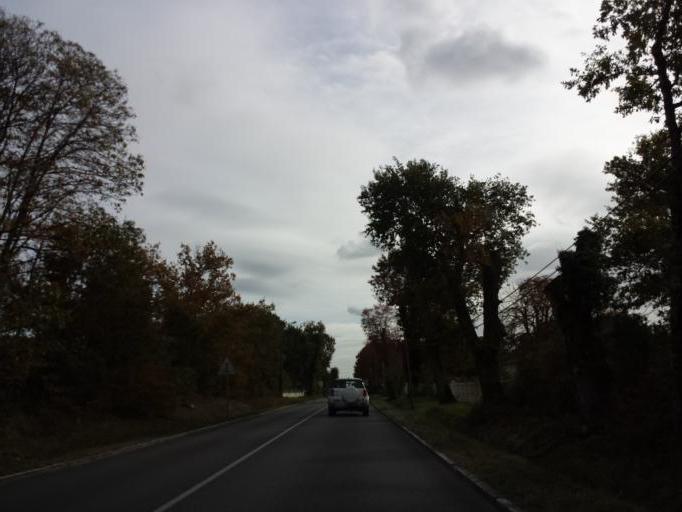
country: FR
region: Aquitaine
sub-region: Departement de la Gironde
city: Marcheprime
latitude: 44.7787
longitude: -0.9311
